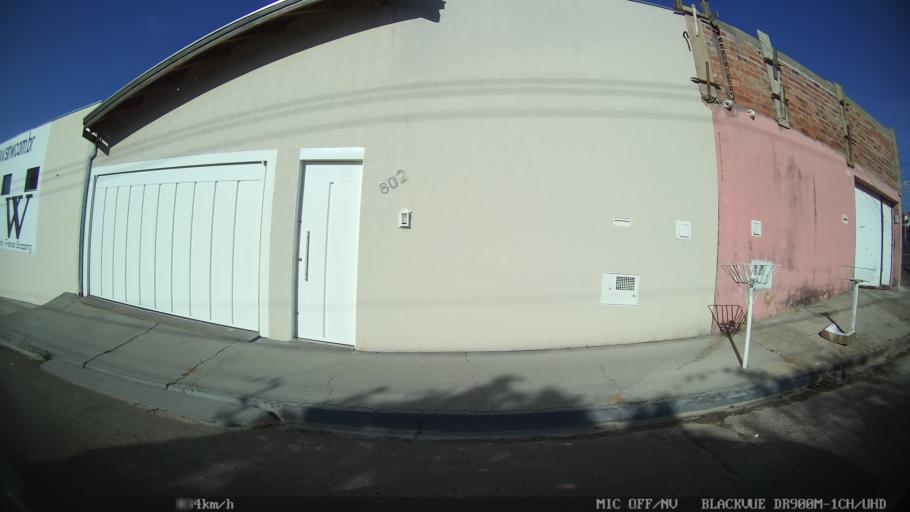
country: BR
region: Sao Paulo
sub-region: Franca
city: Franca
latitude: -20.5114
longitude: -47.4126
